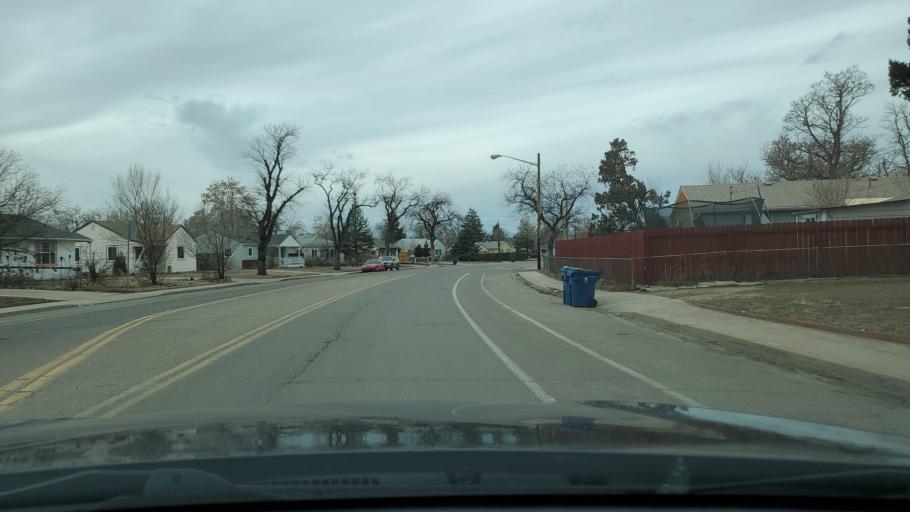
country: US
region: Colorado
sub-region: Adams County
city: Aurora
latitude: 39.7270
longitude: -104.8537
